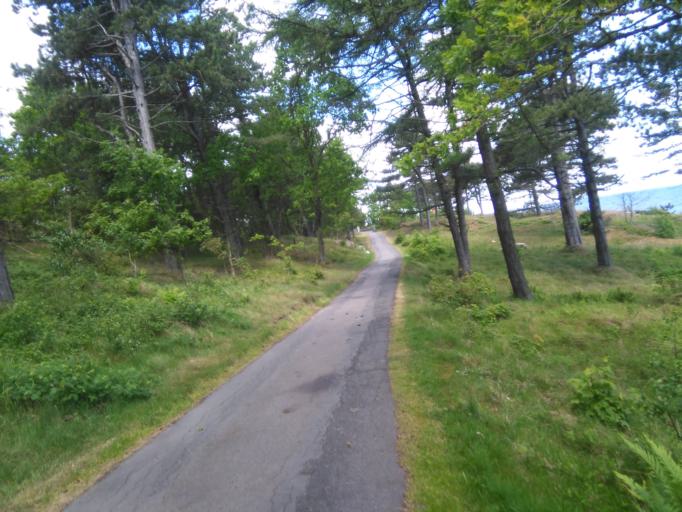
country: DK
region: Capital Region
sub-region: Bornholm Kommune
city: Ronne
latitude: 55.2968
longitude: 14.7757
